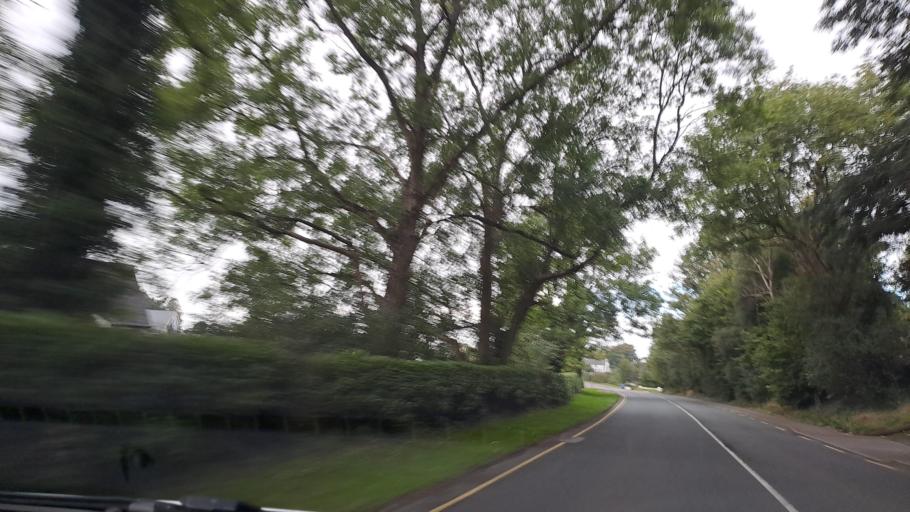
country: IE
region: Ulster
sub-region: County Monaghan
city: Monaghan
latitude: 54.2333
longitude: -6.9629
